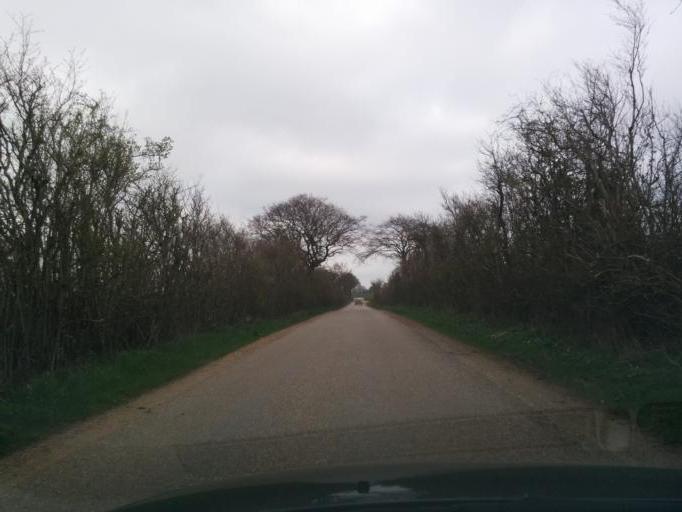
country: DK
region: South Denmark
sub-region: Kolding Kommune
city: Christiansfeld
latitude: 55.3906
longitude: 9.3982
